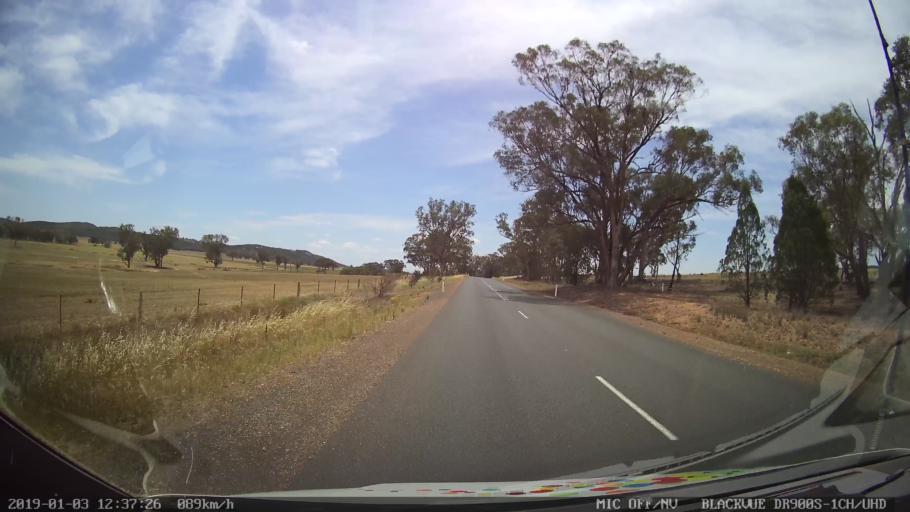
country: AU
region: New South Wales
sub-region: Weddin
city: Grenfell
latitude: -33.8427
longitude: 148.1843
